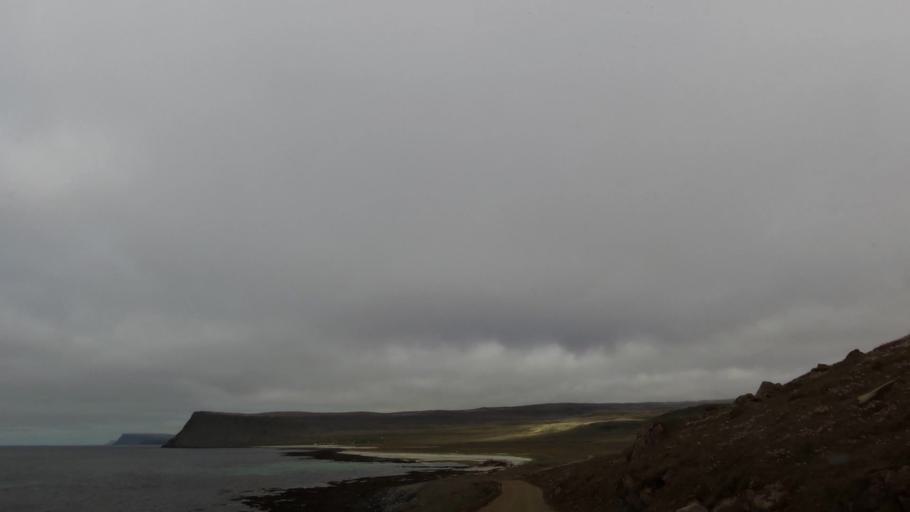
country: IS
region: West
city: Olafsvik
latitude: 65.5121
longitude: -24.5032
